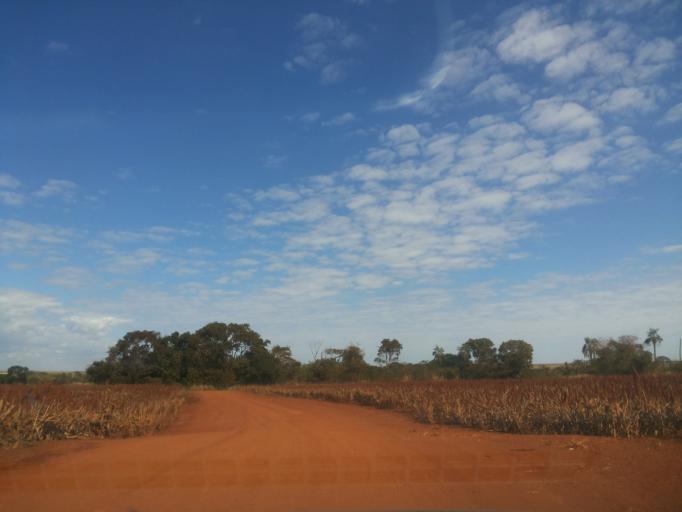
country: BR
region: Minas Gerais
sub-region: Centralina
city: Centralina
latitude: -18.5654
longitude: -49.2253
